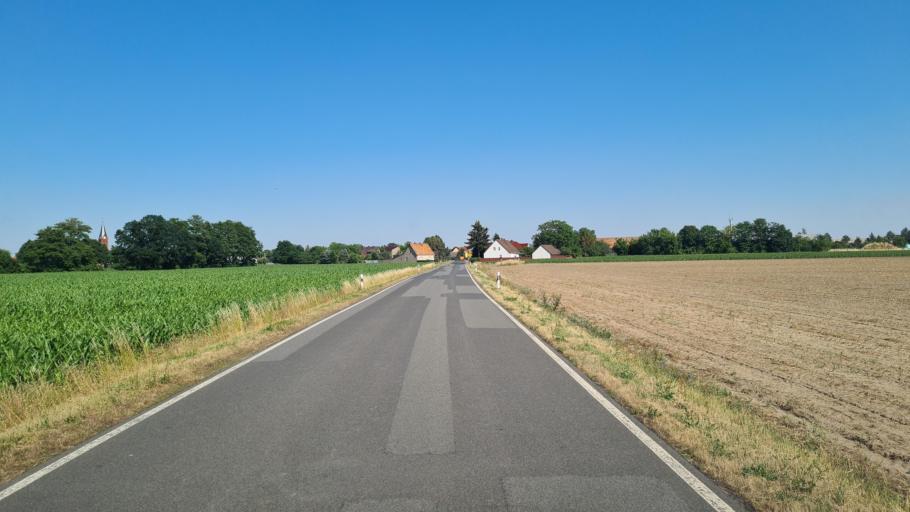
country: DE
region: Saxony-Anhalt
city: Annaburg
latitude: 51.6961
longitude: 12.9877
